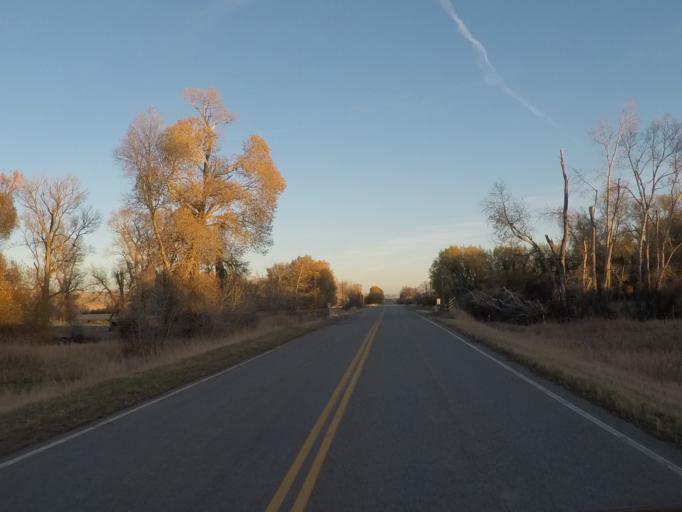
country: US
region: Montana
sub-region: Sweet Grass County
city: Big Timber
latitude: 45.7759
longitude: -109.8067
